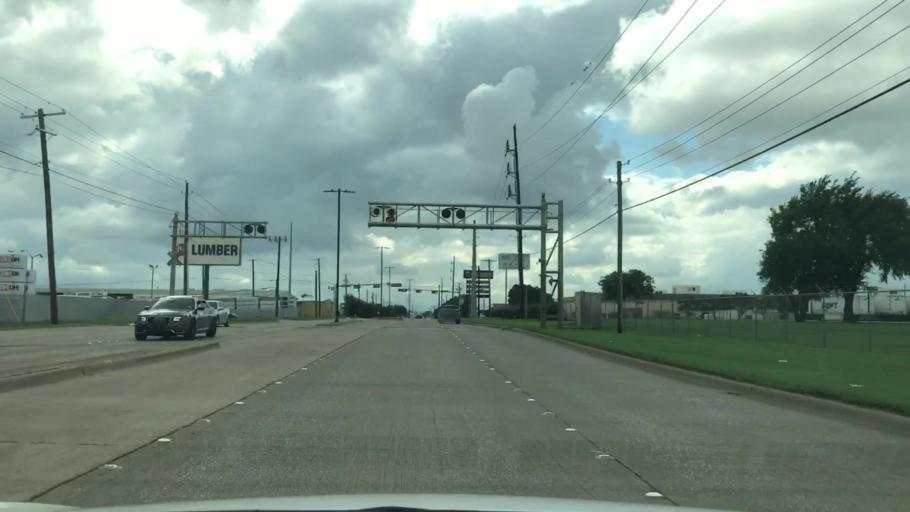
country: US
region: Texas
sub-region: Dallas County
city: Garland
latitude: 32.8945
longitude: -96.6715
